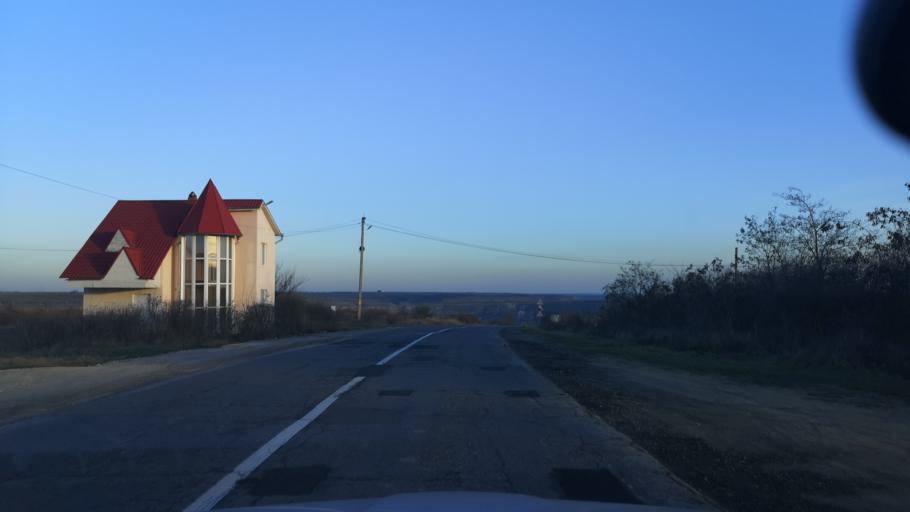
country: MD
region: Telenesti
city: Cocieri
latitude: 47.3113
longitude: 28.9642
